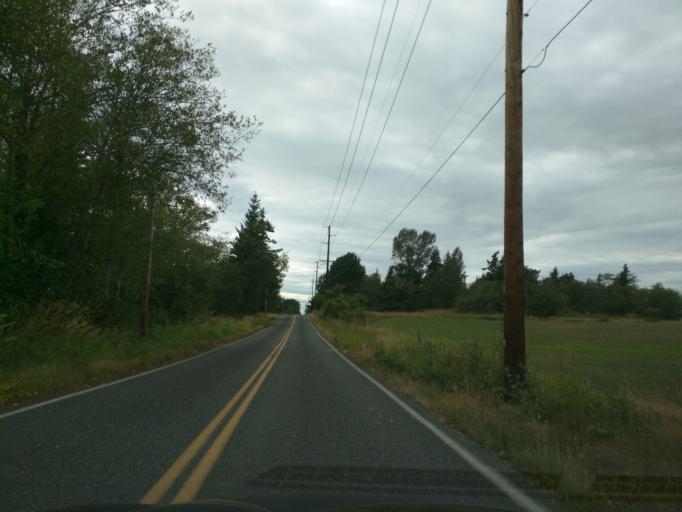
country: US
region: Washington
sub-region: Whatcom County
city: Bellingham
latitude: 48.8148
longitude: -122.4646
